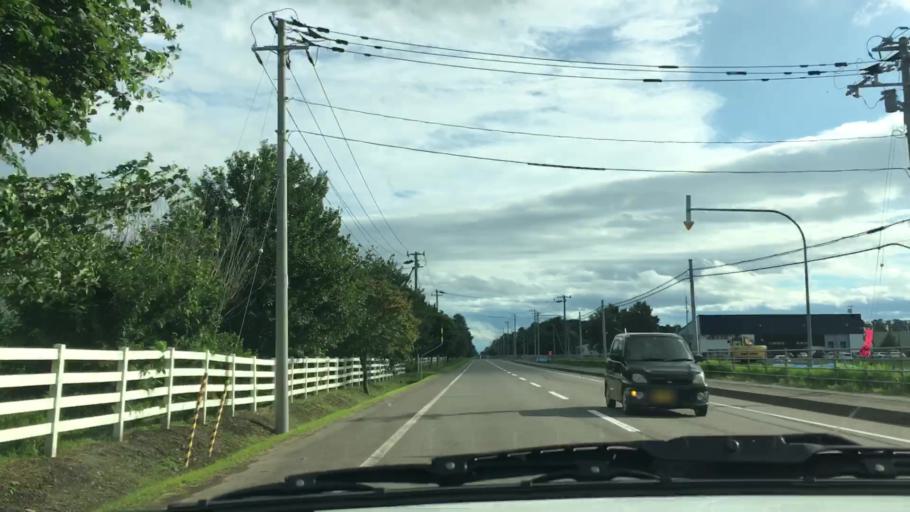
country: JP
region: Hokkaido
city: Otofuke
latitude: 43.2521
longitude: 143.2995
